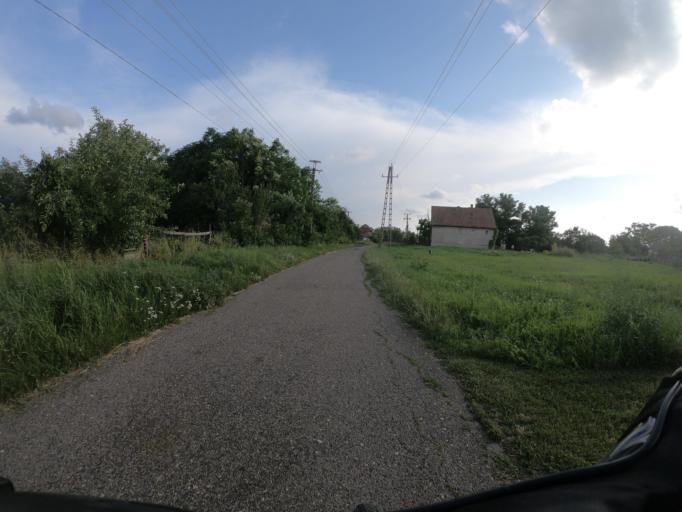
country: HU
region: Borsod-Abauj-Zemplen
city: Mezokeresztes
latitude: 47.8085
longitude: 20.7340
